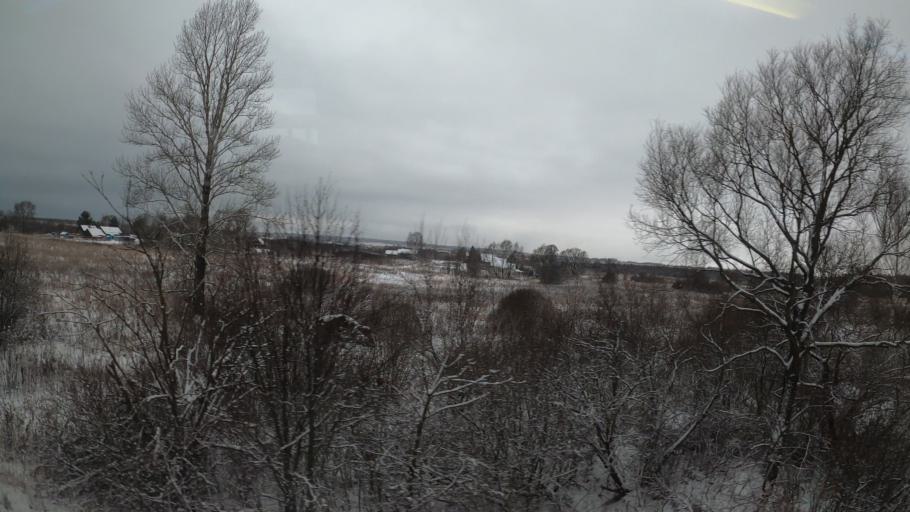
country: RU
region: Jaroslavl
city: Pereslavl'-Zalesskiy
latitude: 56.6839
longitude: 38.9198
